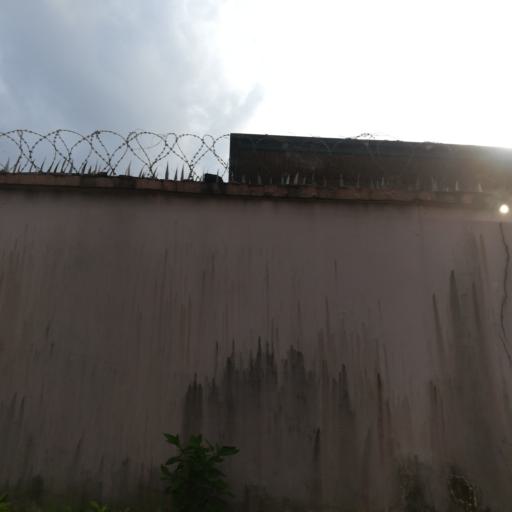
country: NG
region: Rivers
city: Port Harcourt
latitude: 4.8426
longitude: 7.0538
